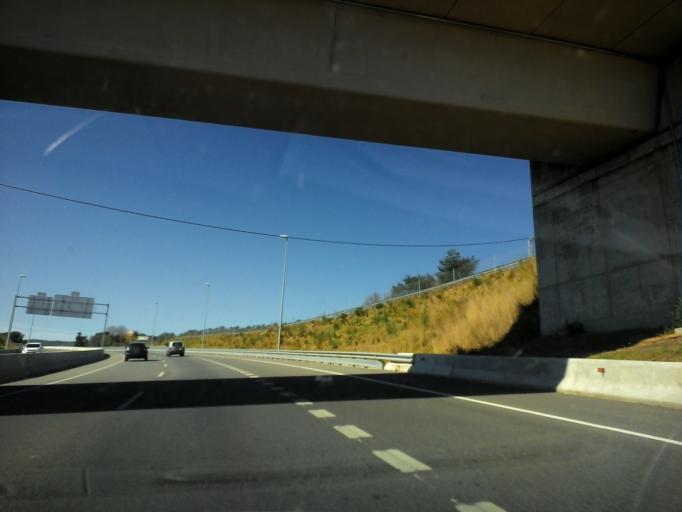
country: ES
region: Catalonia
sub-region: Provincia de Girona
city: Palamos
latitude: 41.8600
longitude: 3.1152
